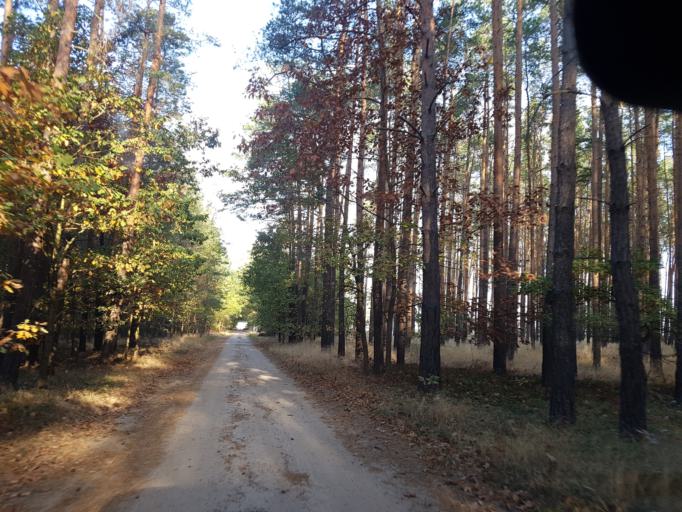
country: DE
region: Brandenburg
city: Finsterwalde
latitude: 51.5962
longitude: 13.6843
